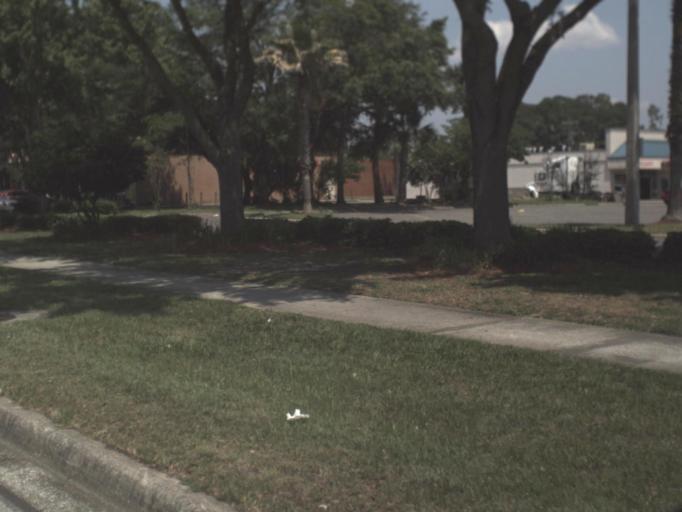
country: US
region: Florida
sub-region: Duval County
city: Jacksonville
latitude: 30.3092
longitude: -81.7362
